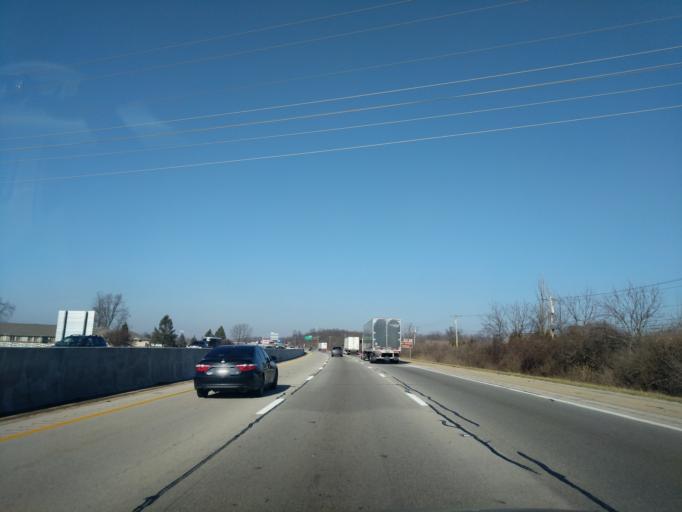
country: US
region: Ohio
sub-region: Miami County
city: Tipp City
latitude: 39.9742
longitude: -84.1906
